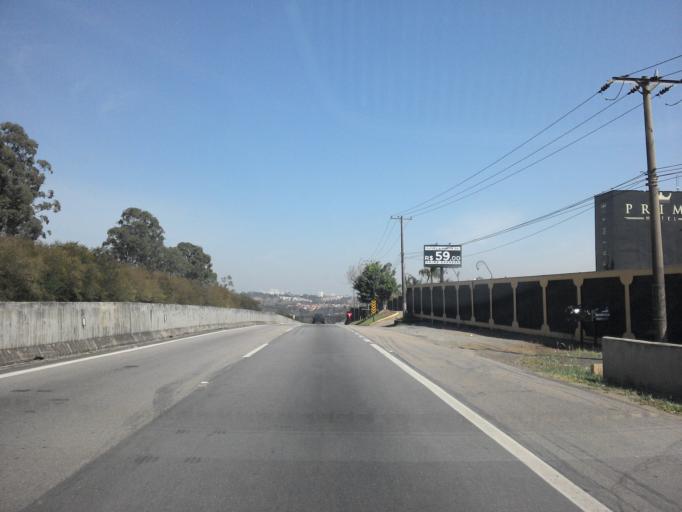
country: BR
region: Sao Paulo
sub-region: Campinas
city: Campinas
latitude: -22.8932
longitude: -47.1297
